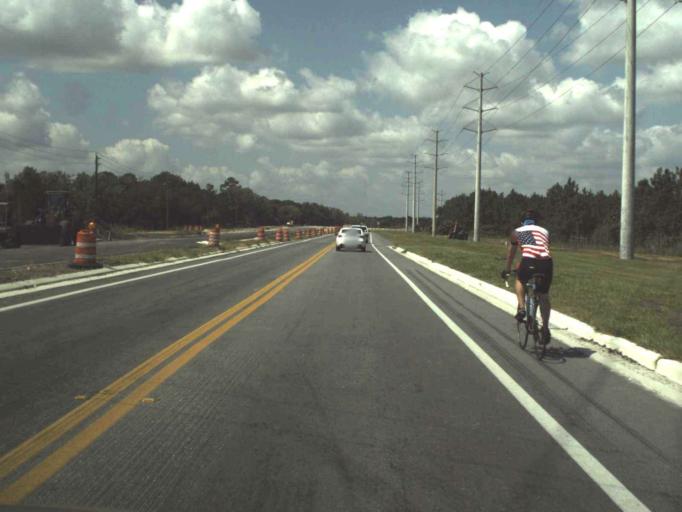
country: US
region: Florida
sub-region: Seminole County
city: Midway
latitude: 28.8207
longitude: -81.1852
